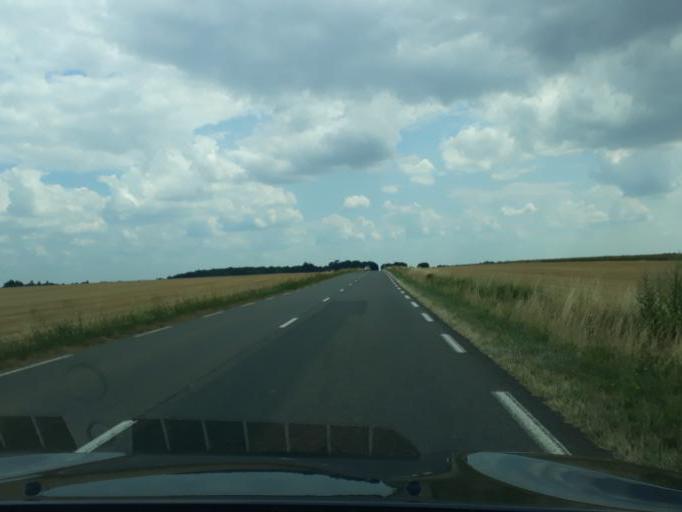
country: FR
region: Centre
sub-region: Departement du Cher
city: Avord
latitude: 47.0275
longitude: 2.6633
